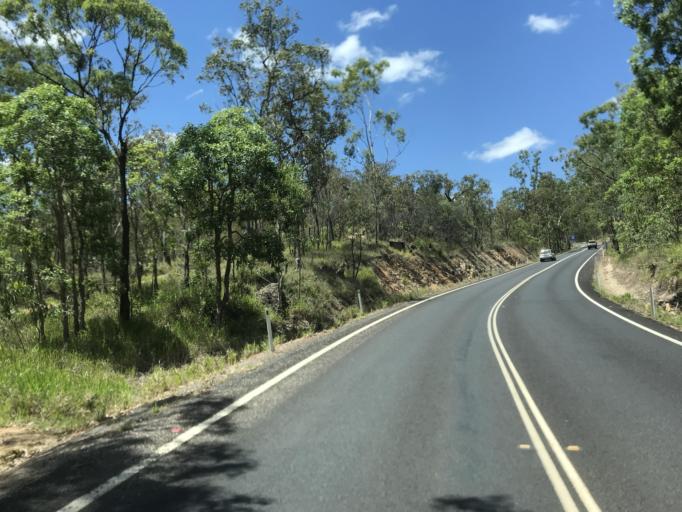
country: AU
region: Queensland
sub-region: Tablelands
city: Atherton
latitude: -17.4016
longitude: 145.3899
